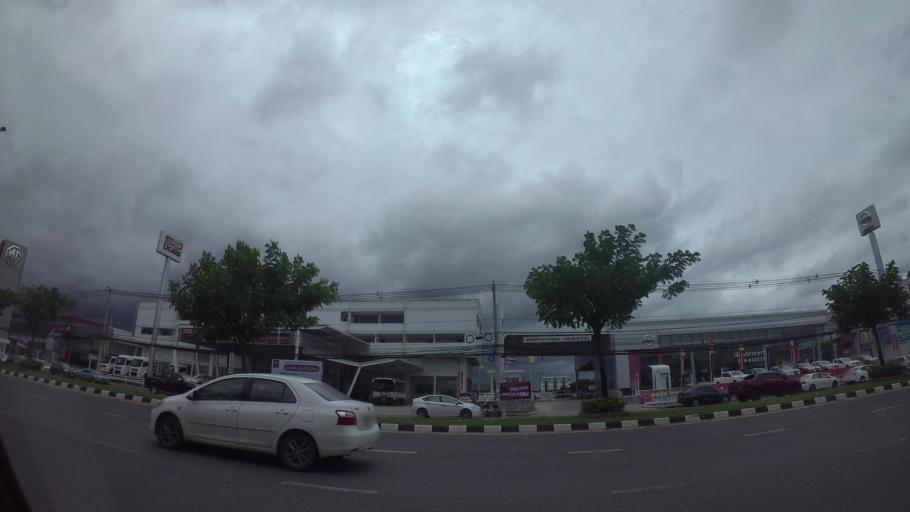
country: TH
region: Rayong
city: Rayong
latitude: 12.6882
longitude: 101.2651
